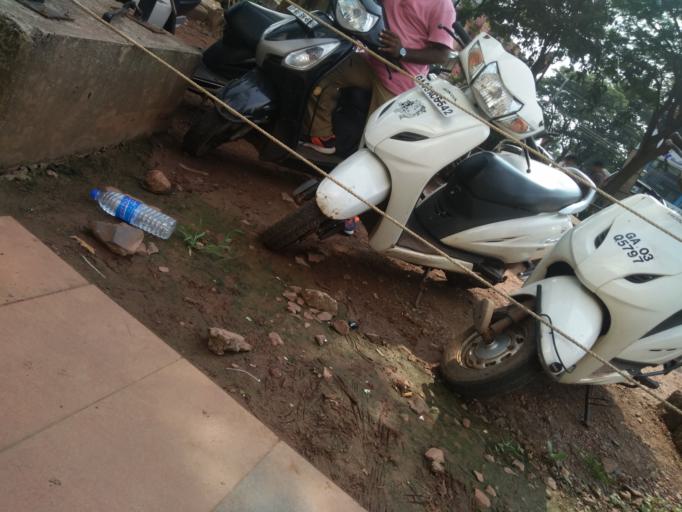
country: IN
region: Goa
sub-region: North Goa
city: Serula
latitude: 15.5260
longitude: 73.8269
